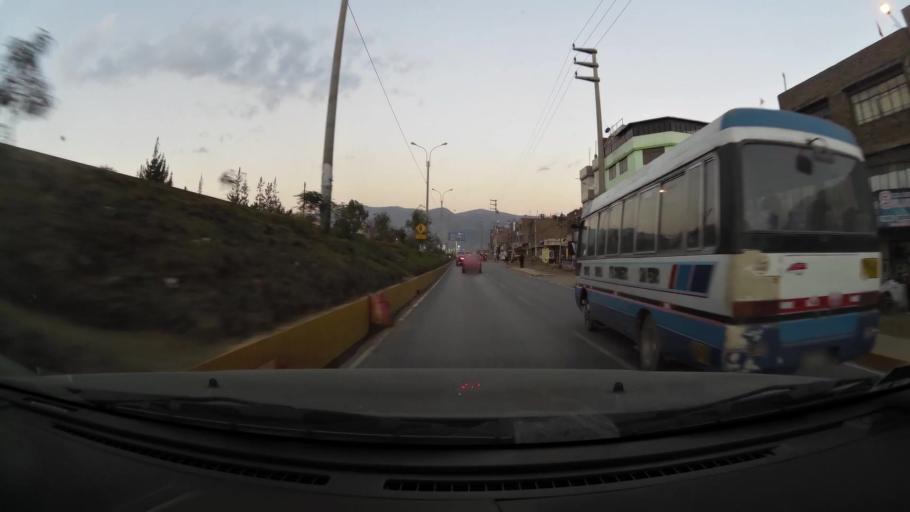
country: PE
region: Junin
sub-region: Provincia de Huancayo
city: El Tambo
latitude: -12.0533
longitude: -75.2308
